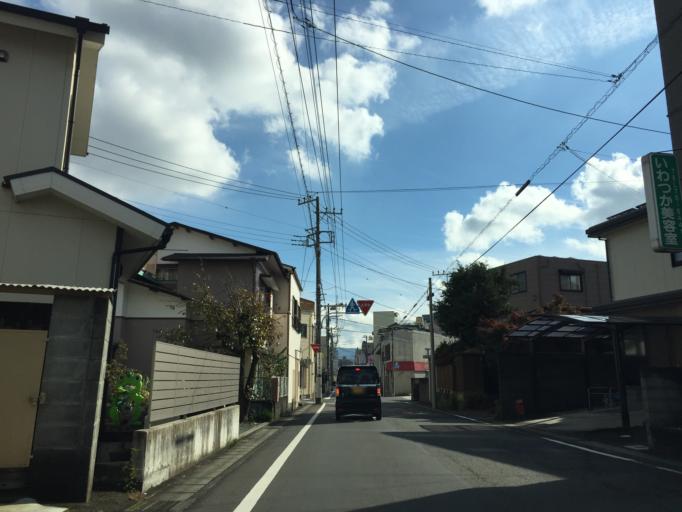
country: JP
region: Shizuoka
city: Mishima
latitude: 35.1231
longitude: 138.9066
